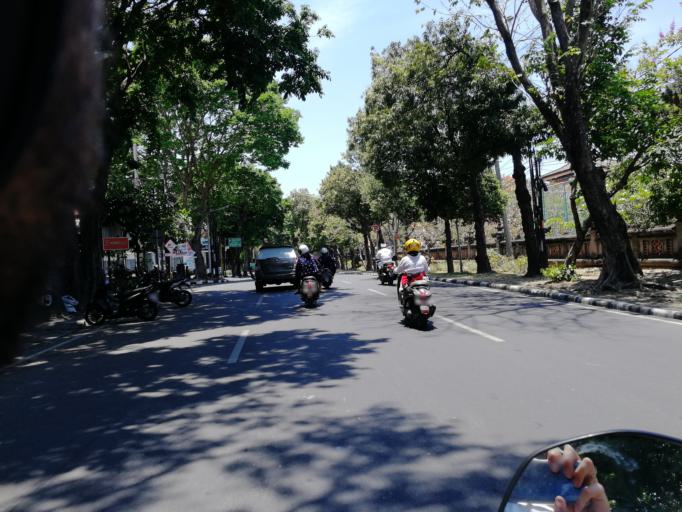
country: ID
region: Bali
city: Denpasar
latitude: -8.6672
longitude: 115.2309
